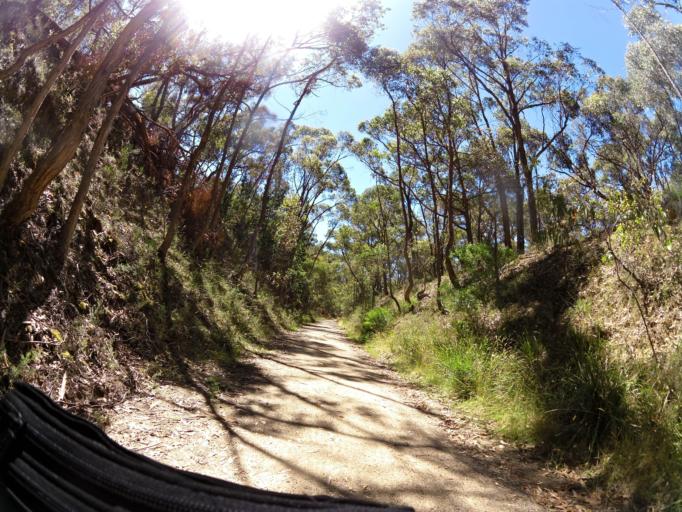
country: AU
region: Victoria
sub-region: Ballarat North
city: Delacombe
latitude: -37.7088
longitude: 143.6089
